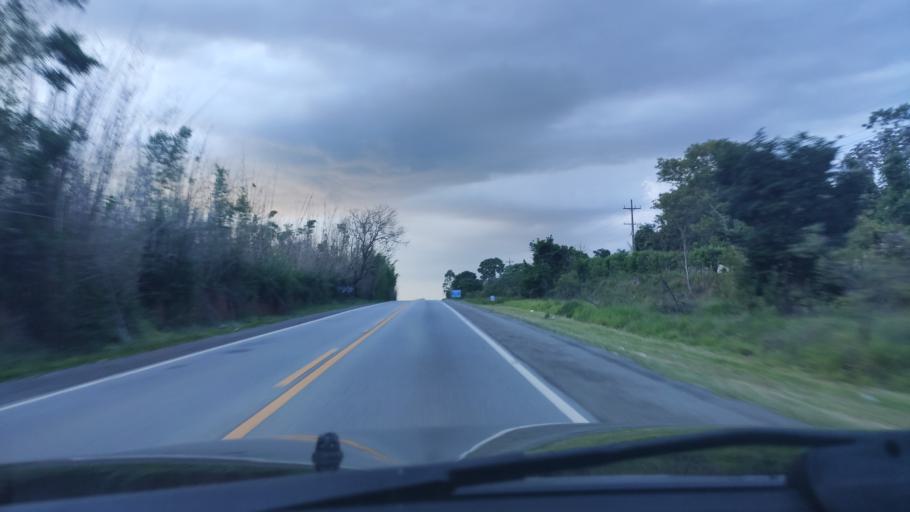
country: BR
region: Sao Paulo
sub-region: Braganca Paulista
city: Braganca Paulista
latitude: -22.8675
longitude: -46.5359
